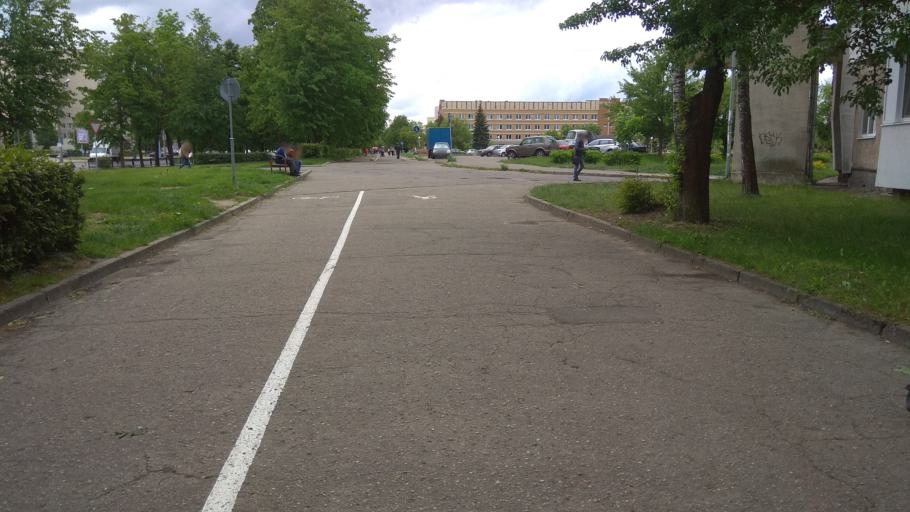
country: BY
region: Grodnenskaya
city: Hrodna
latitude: 53.7048
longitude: 23.8055
